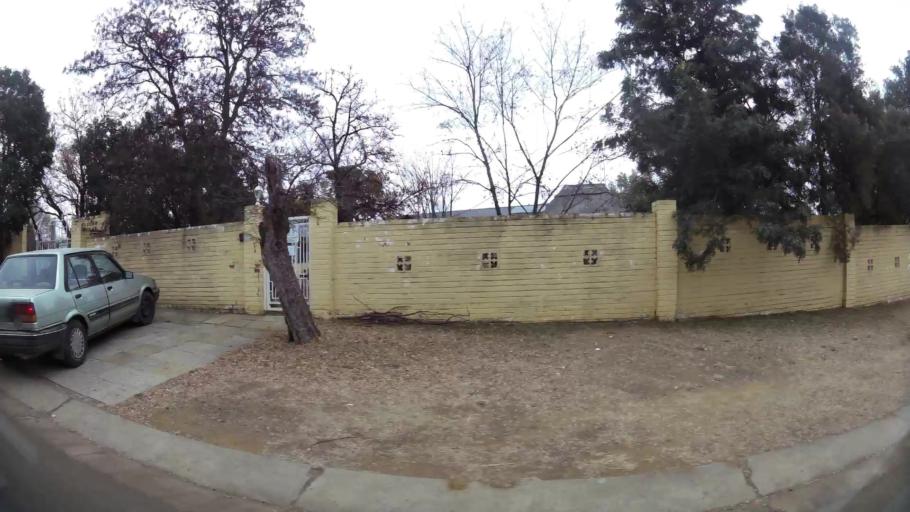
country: ZA
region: Orange Free State
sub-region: Fezile Dabi District Municipality
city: Kroonstad
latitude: -27.6837
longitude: 27.2345
